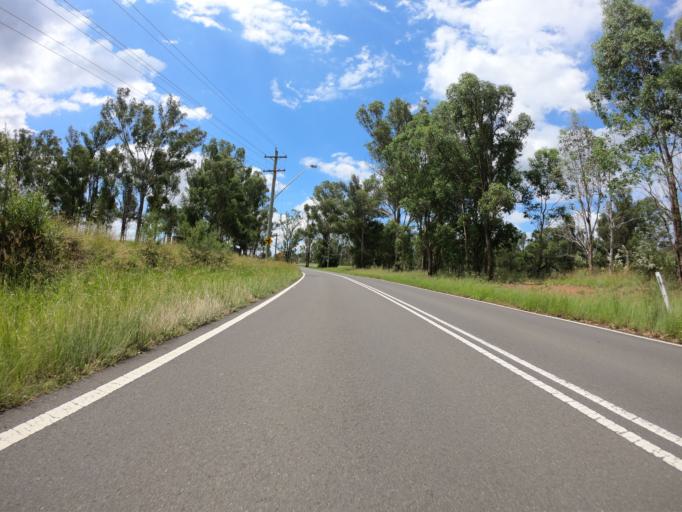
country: AU
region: New South Wales
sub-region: Penrith Municipality
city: Mulgoa
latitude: -33.8285
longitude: 150.6643
